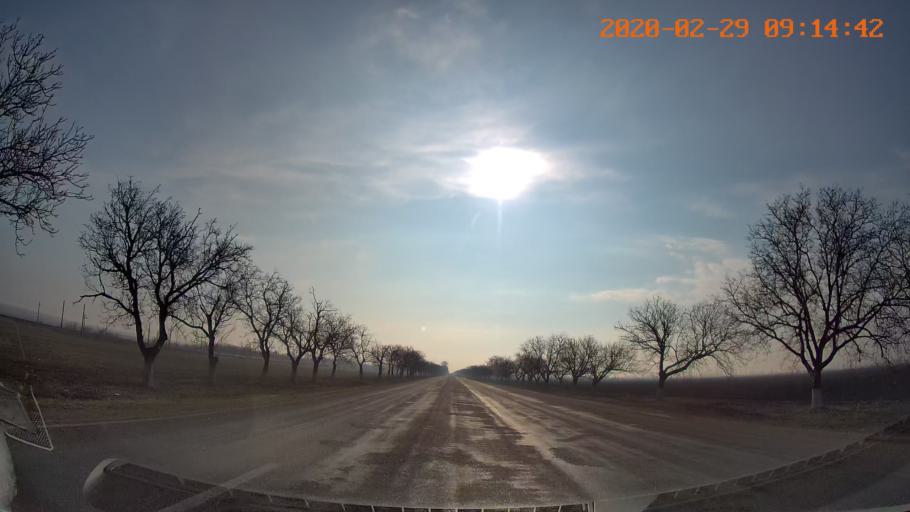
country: MD
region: Telenesti
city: Pervomaisc
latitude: 46.8065
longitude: 29.8573
